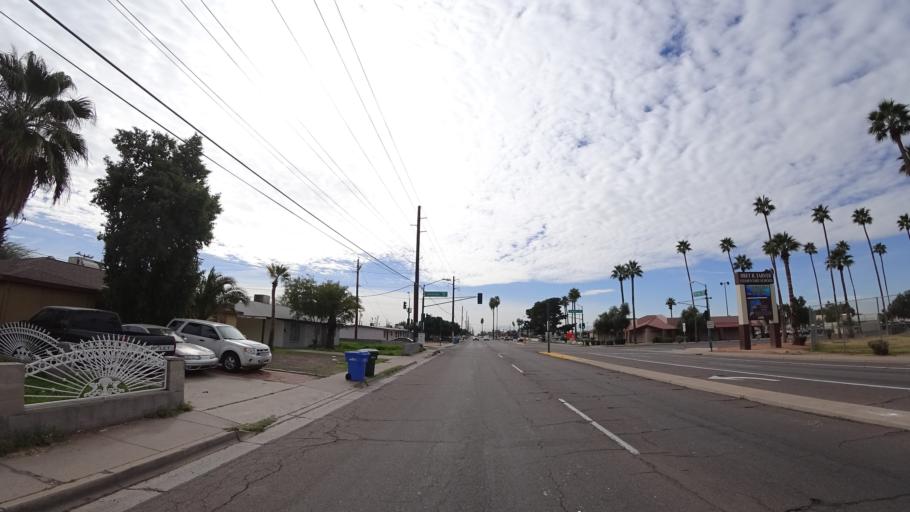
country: US
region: Arizona
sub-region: Maricopa County
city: Glendale
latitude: 33.4989
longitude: -112.1688
